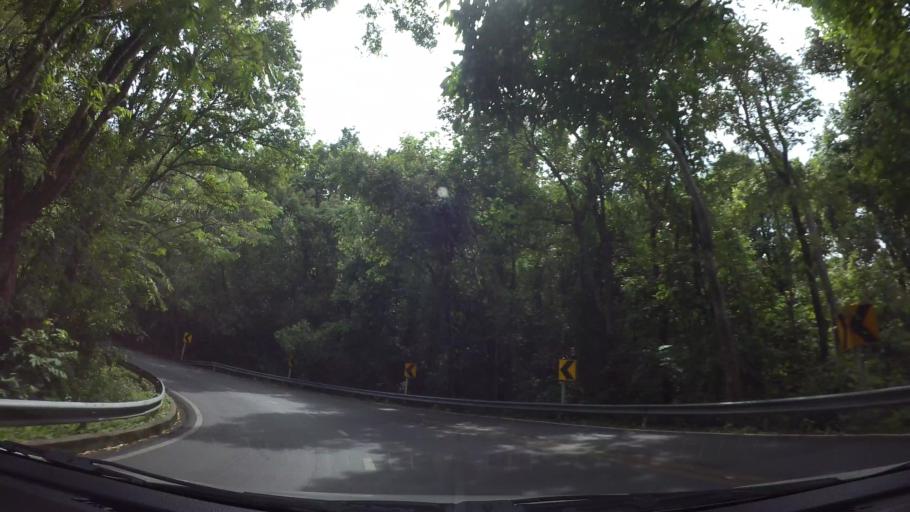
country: TH
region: Chiang Mai
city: Chiang Mai
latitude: 18.7939
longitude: 98.9289
